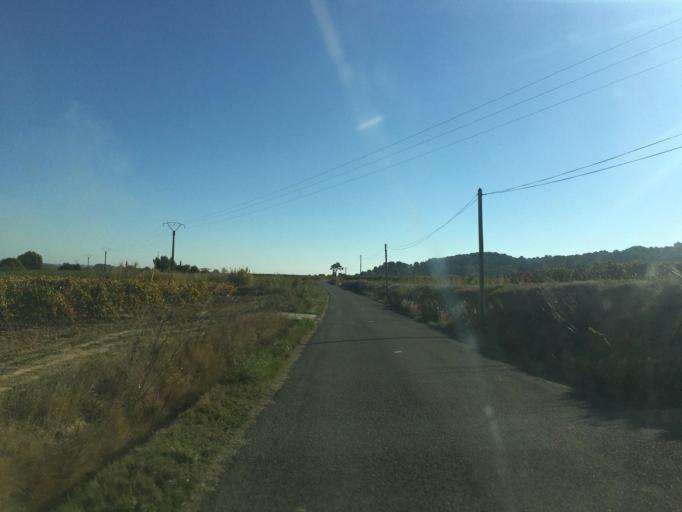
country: FR
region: Languedoc-Roussillon
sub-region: Departement de l'Aude
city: Fleury
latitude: 43.2348
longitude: 3.1509
